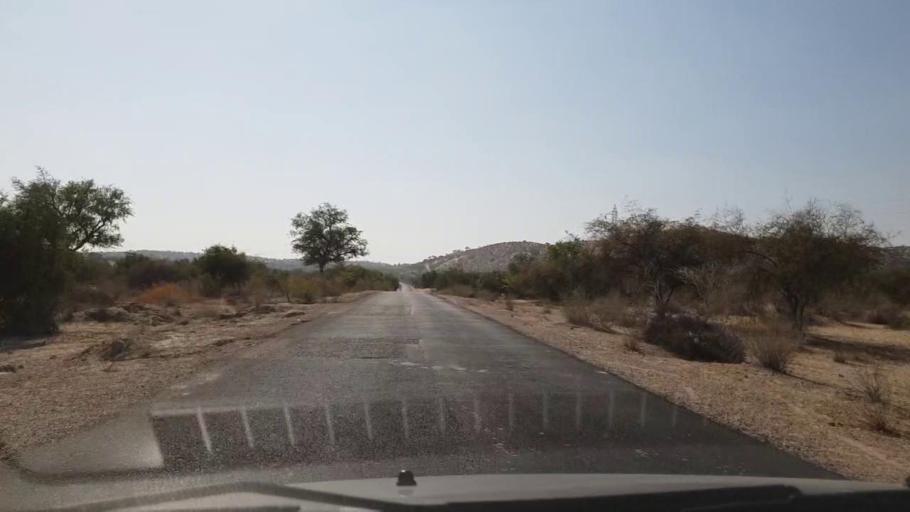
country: PK
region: Sindh
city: Mithi
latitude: 24.6460
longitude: 69.7480
